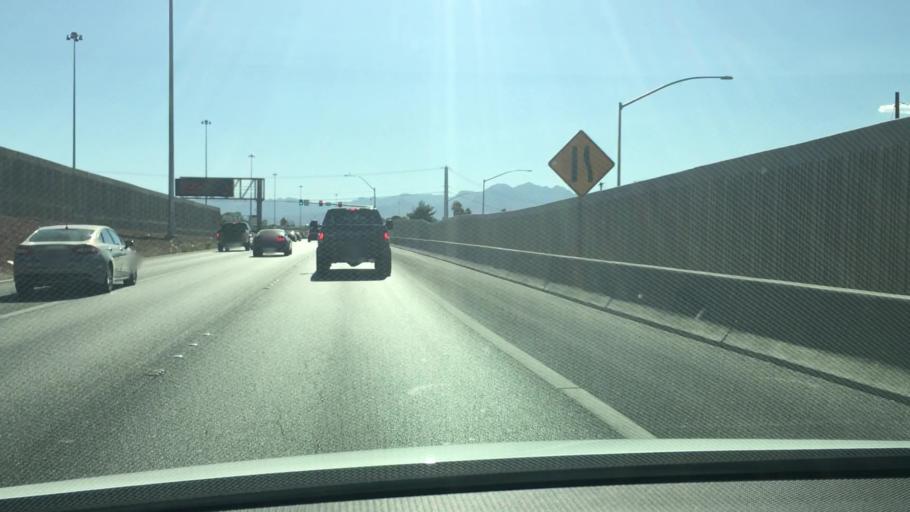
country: US
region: Nevada
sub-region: Clark County
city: Las Vegas
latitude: 36.1757
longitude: -115.1767
